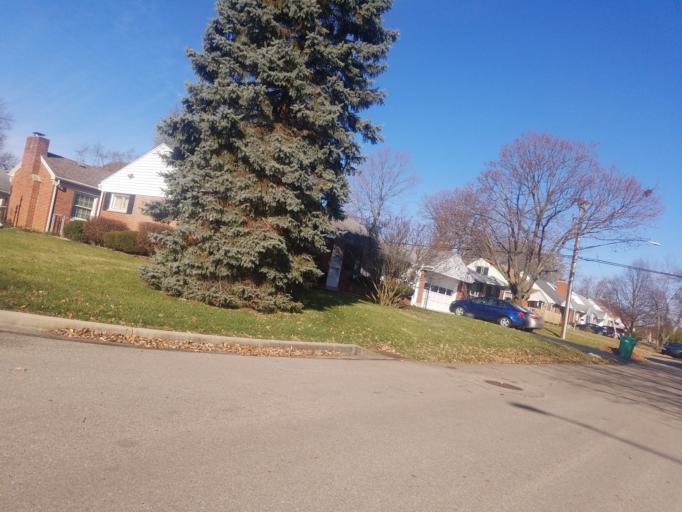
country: US
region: Ohio
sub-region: Montgomery County
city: Kettering
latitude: 39.7066
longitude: -84.1533
